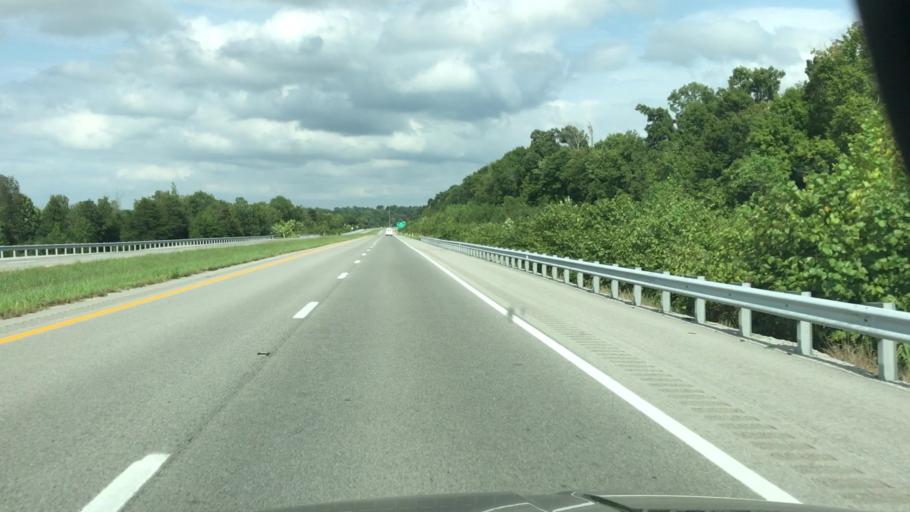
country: US
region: Kentucky
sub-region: Hopkins County
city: Dawson Springs
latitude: 37.1912
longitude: -87.7081
